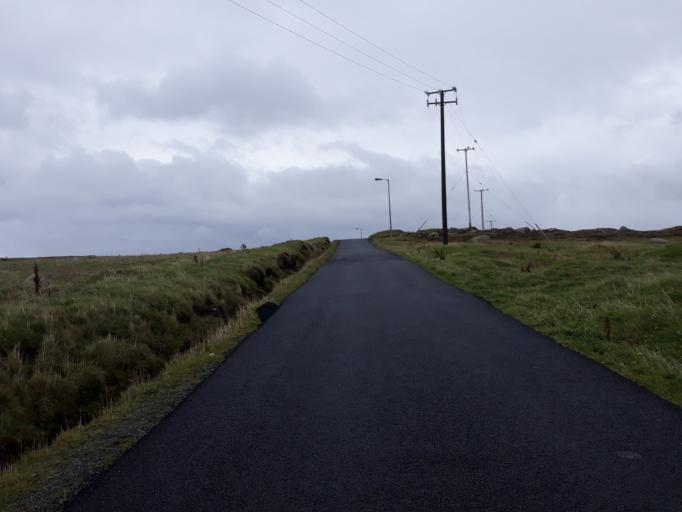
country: IE
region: Ulster
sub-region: County Donegal
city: Derrybeg
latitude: 55.2636
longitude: -8.2206
